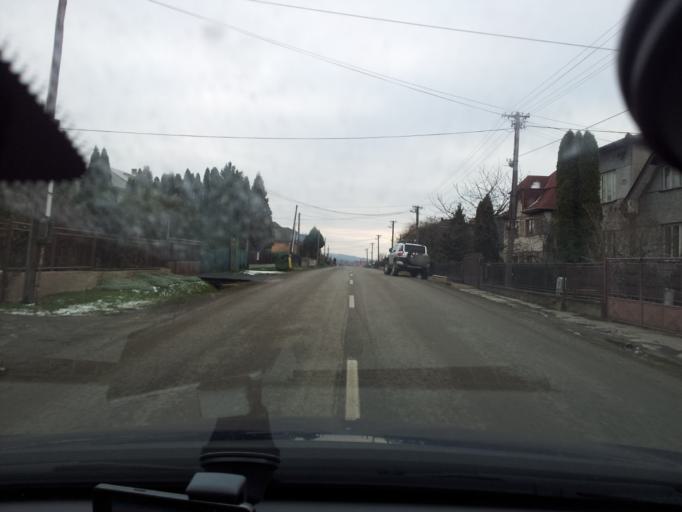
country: SK
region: Kosicky
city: Kosice
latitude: 48.7471
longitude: 21.3444
